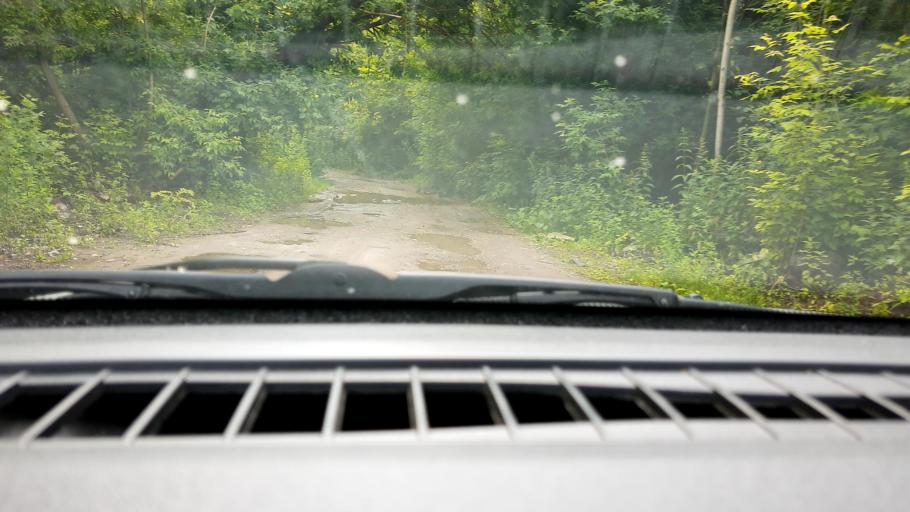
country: RU
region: Nizjnij Novgorod
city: Neklyudovo
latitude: 56.3972
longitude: 43.8491
